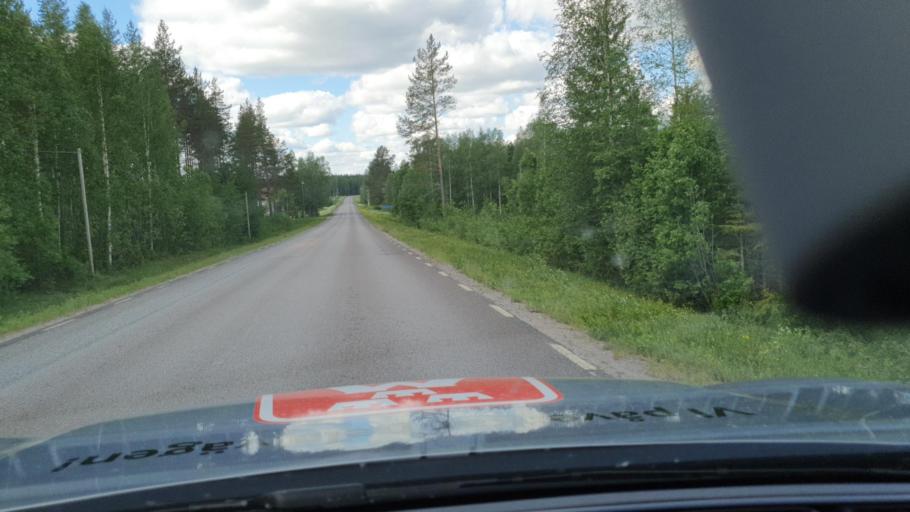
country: SE
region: Norrbotten
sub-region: Pitea Kommun
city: Rosvik
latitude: 65.5138
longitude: 21.5966
